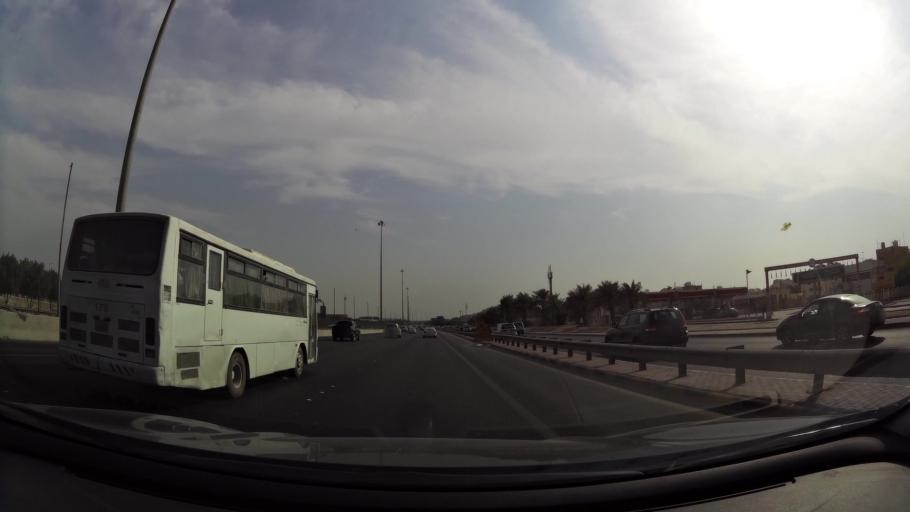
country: KW
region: Al Farwaniyah
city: Janub as Surrah
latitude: 29.2928
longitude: 47.9823
